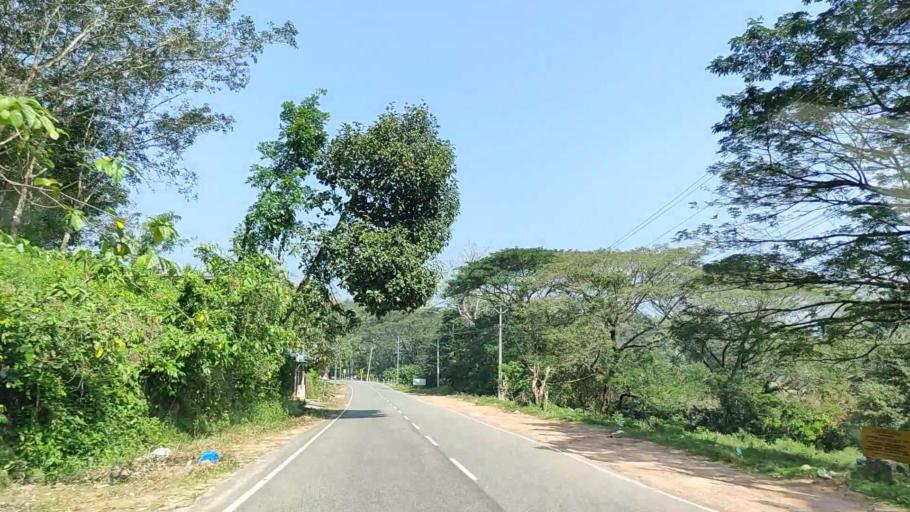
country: IN
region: Kerala
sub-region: Kollam
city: Punalur
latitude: 8.9268
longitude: 77.0646
